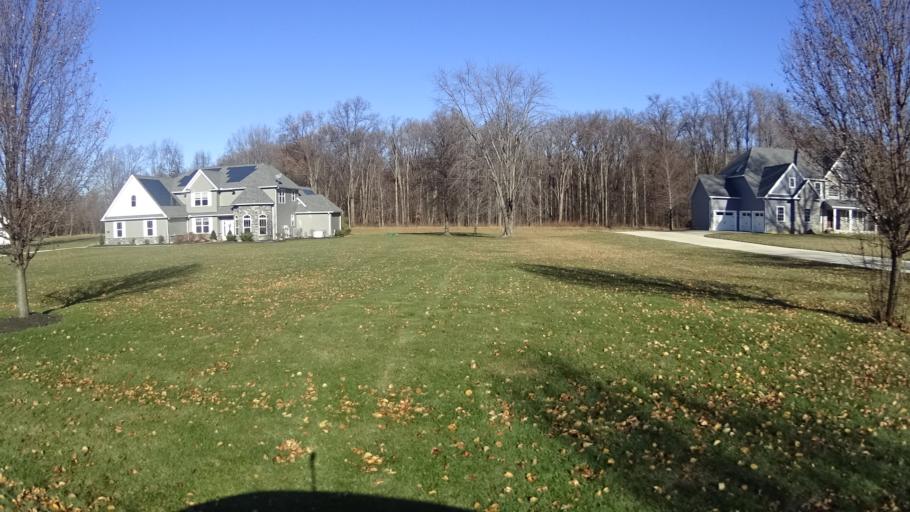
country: US
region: Ohio
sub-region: Lorain County
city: South Amherst
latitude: 41.3782
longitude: -82.2893
